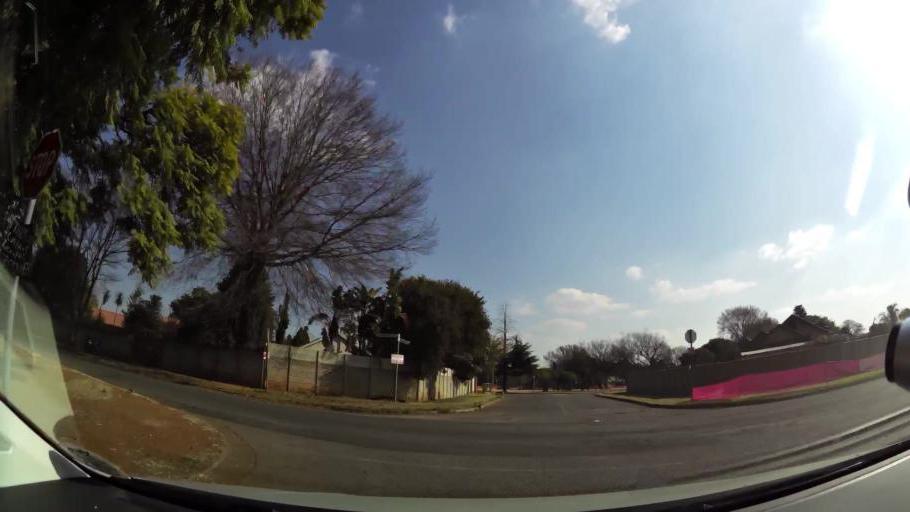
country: ZA
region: Gauteng
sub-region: City of Johannesburg Metropolitan Municipality
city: Modderfontein
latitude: -26.0898
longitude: 28.2100
